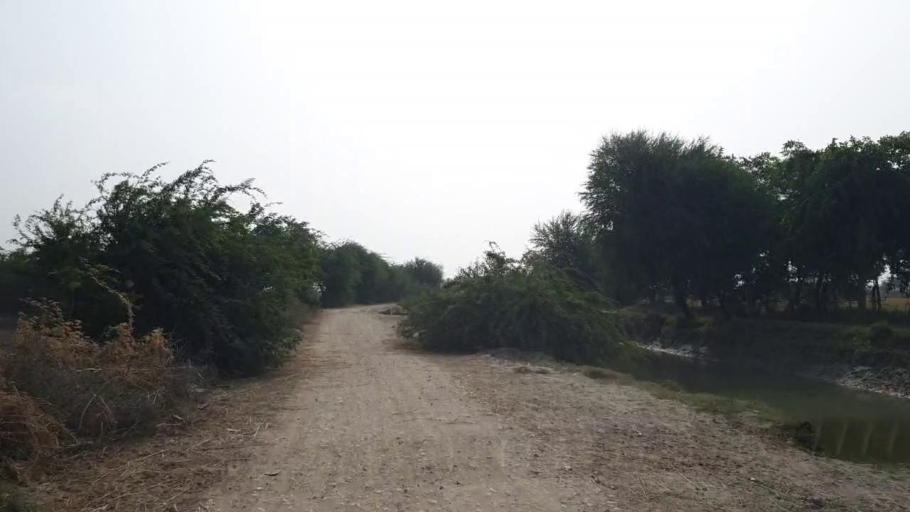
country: PK
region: Sindh
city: Kario
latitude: 24.7922
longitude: 68.5620
